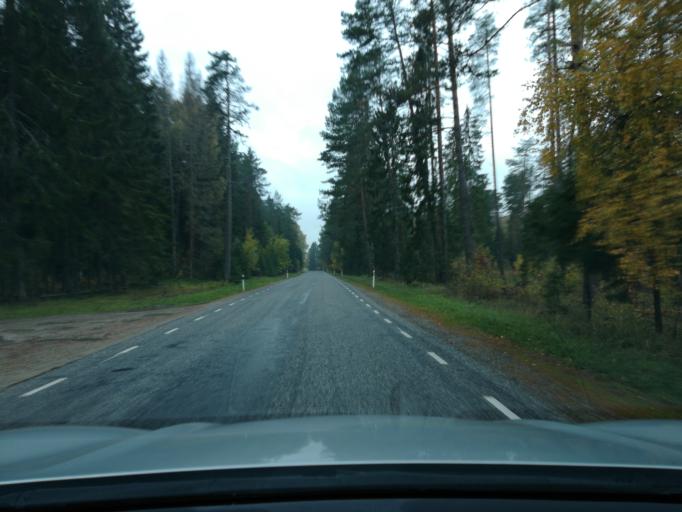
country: EE
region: Ida-Virumaa
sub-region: Johvi vald
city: Johvi
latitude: 59.1534
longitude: 27.3859
